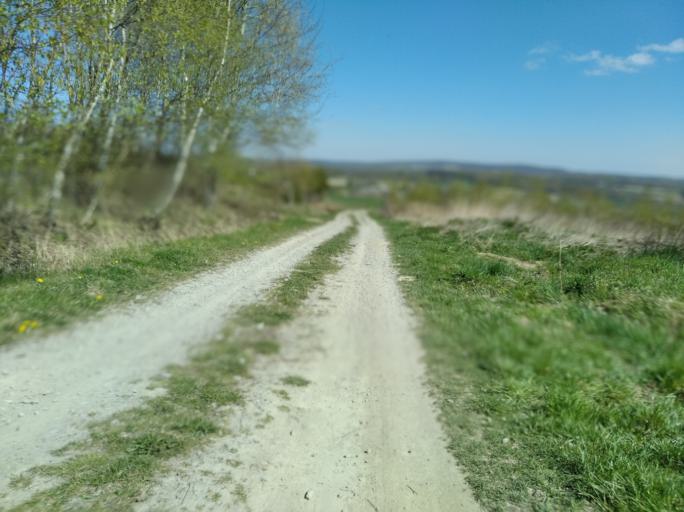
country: PL
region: Subcarpathian Voivodeship
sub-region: Powiat strzyzowski
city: Wisniowa
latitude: 49.9072
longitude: 21.6530
